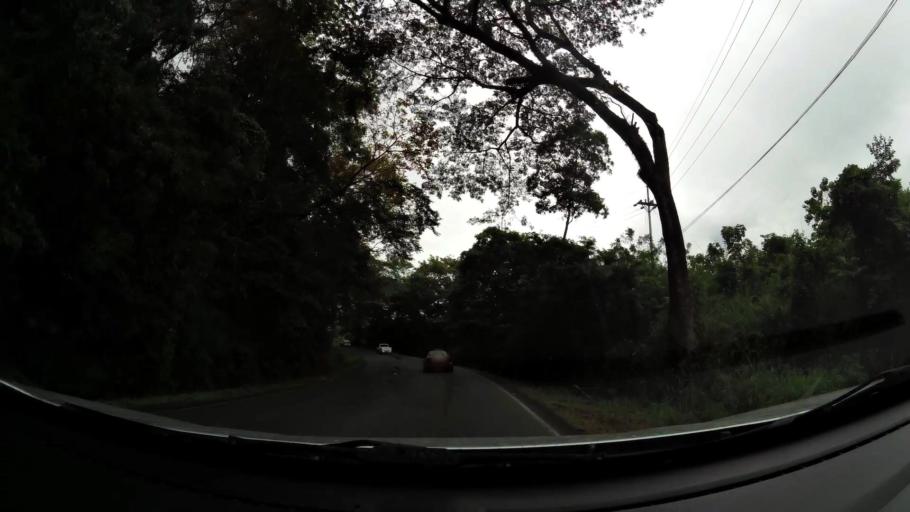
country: CR
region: Puntarenas
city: Esparza
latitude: 9.9980
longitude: -84.6878
